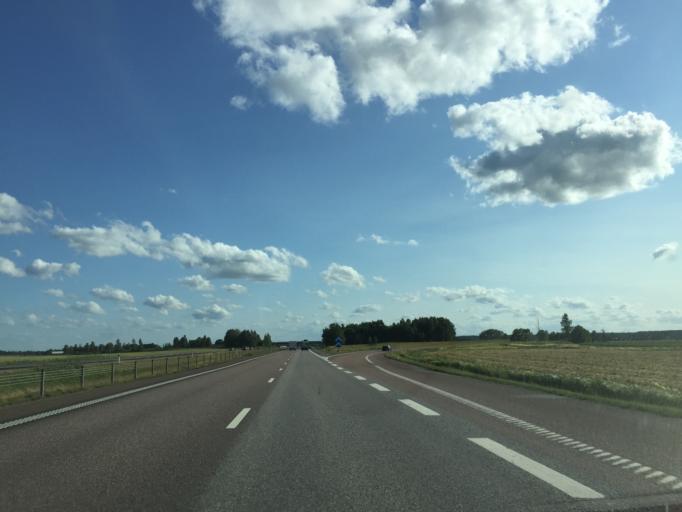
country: SE
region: OErebro
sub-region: Kumla Kommun
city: Kumla
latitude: 59.1723
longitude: 15.1155
